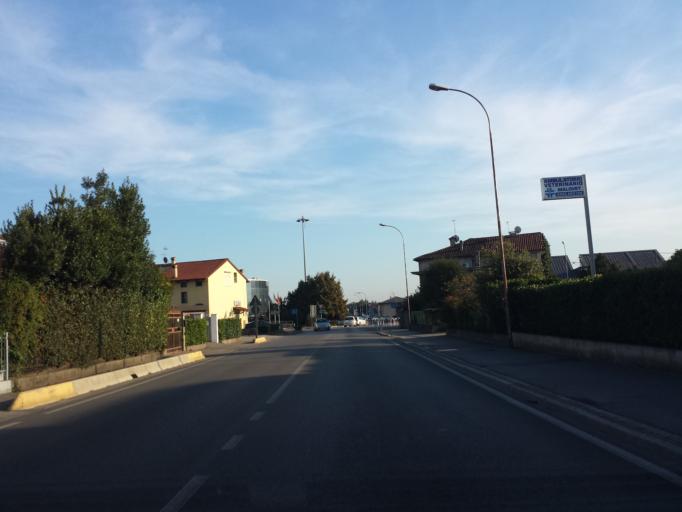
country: IT
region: Veneto
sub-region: Provincia di Vicenza
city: Malo
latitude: 45.6590
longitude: 11.4137
